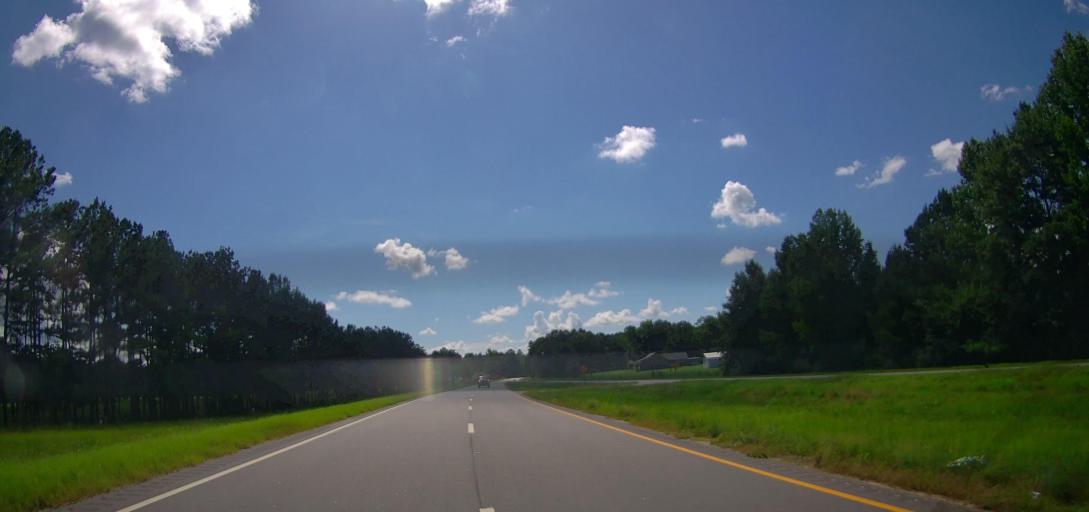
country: US
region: Alabama
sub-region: Macon County
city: Tuskegee
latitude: 32.3782
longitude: -85.7813
